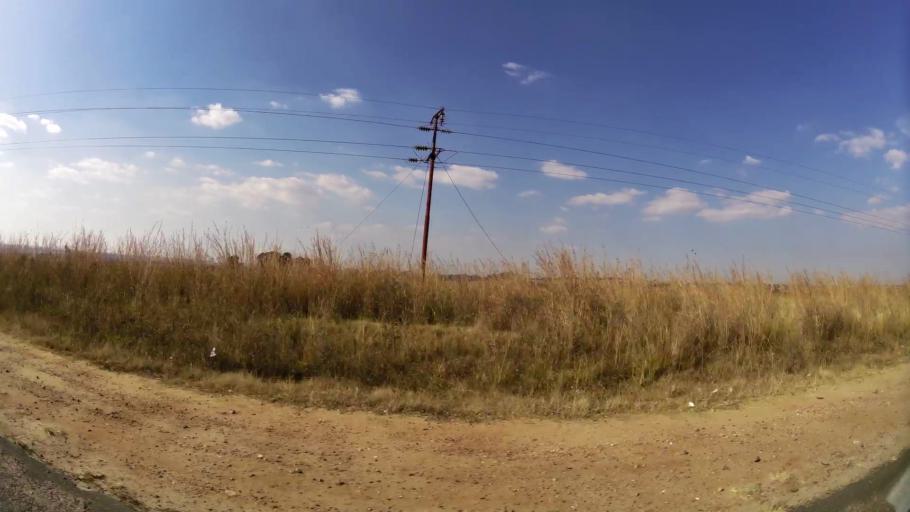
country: ZA
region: Gauteng
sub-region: Ekurhuleni Metropolitan Municipality
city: Tembisa
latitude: -26.0464
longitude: 28.2538
